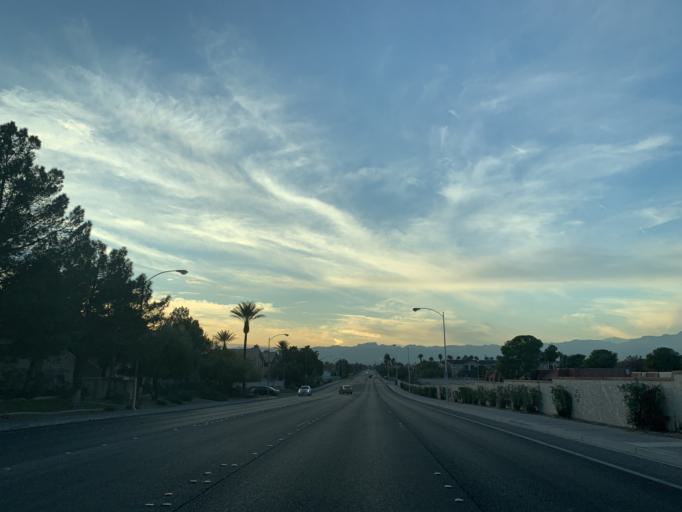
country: US
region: Nevada
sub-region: Clark County
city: Spring Valley
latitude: 36.1079
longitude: -115.2141
